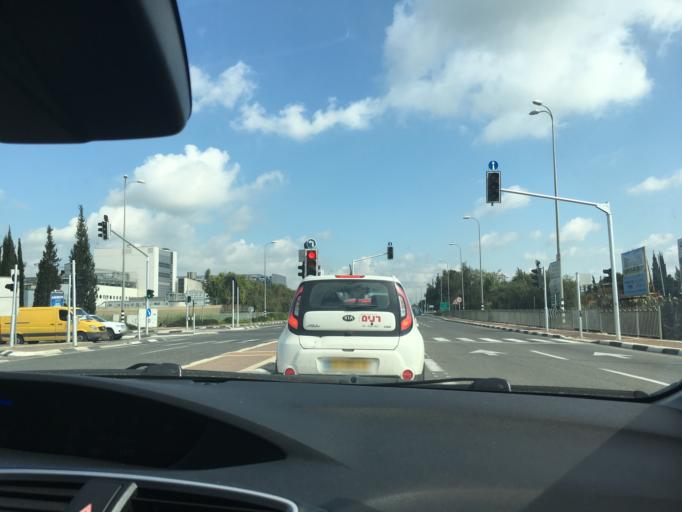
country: IL
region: Central District
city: Jaljulya
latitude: 32.1753
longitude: 34.9357
